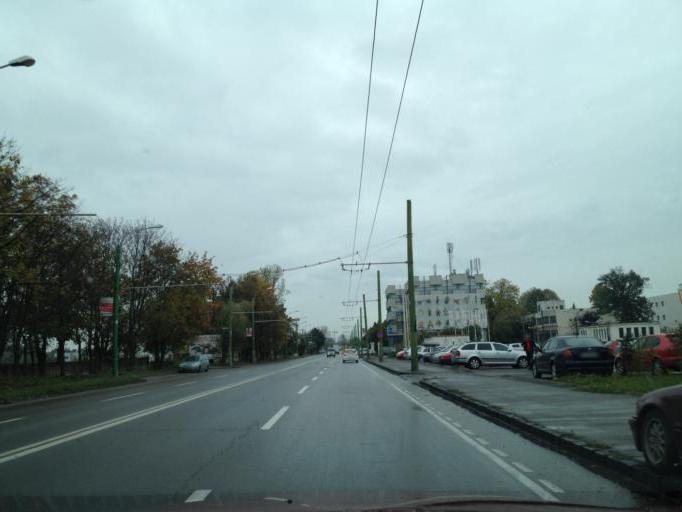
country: RO
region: Brasov
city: Brasov
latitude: 45.6780
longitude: 25.6139
